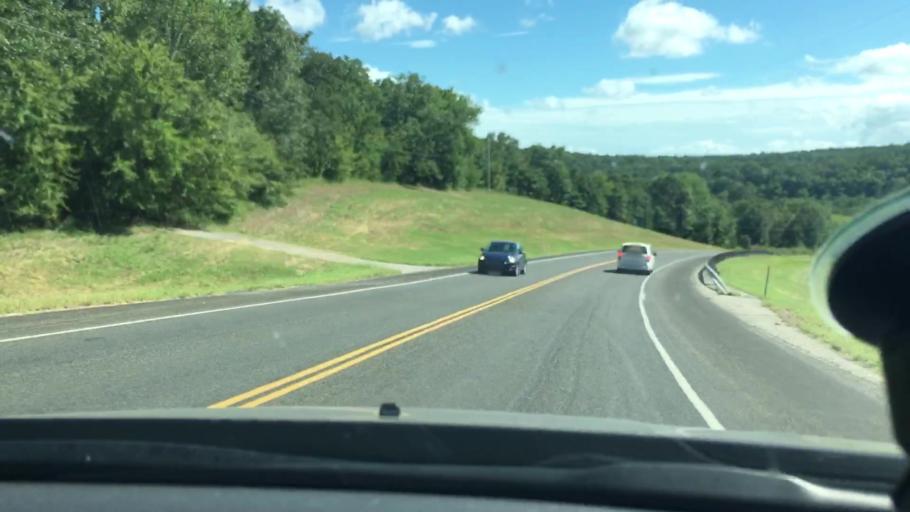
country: US
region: Oklahoma
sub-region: Sequoyah County
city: Vian
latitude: 35.5433
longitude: -94.9686
